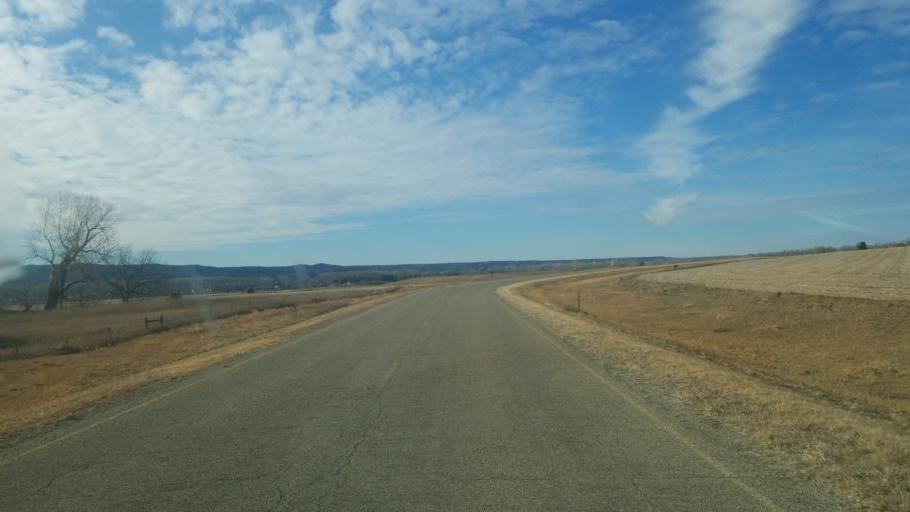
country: US
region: South Dakota
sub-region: Charles Mix County
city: Wagner
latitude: 42.9182
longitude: -98.3714
